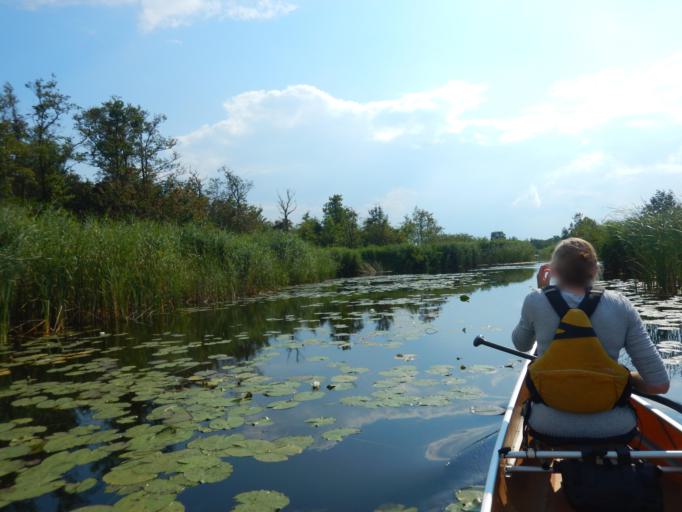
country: NL
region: North Holland
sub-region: Gemeente Wijdemeren
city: Kortenhoef
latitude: 52.2393
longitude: 5.0882
